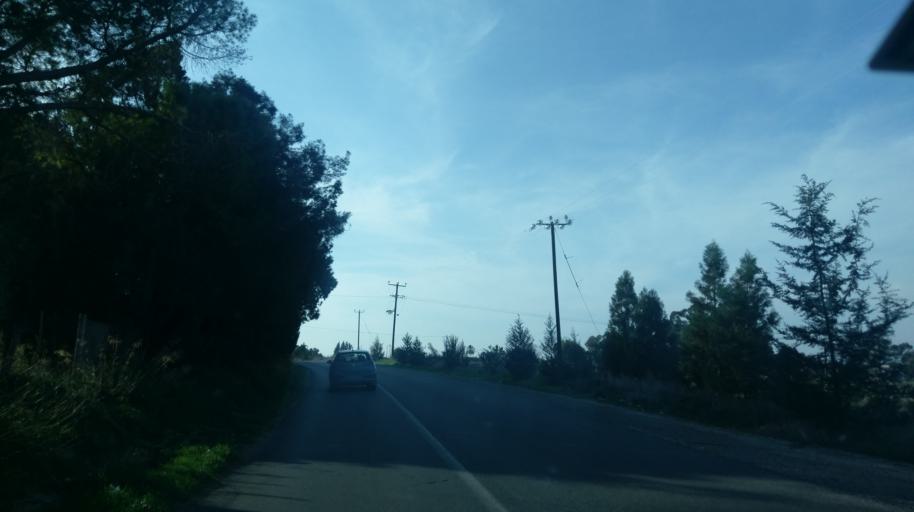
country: CY
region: Larnaka
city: Pergamos
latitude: 35.1108
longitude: 33.7321
